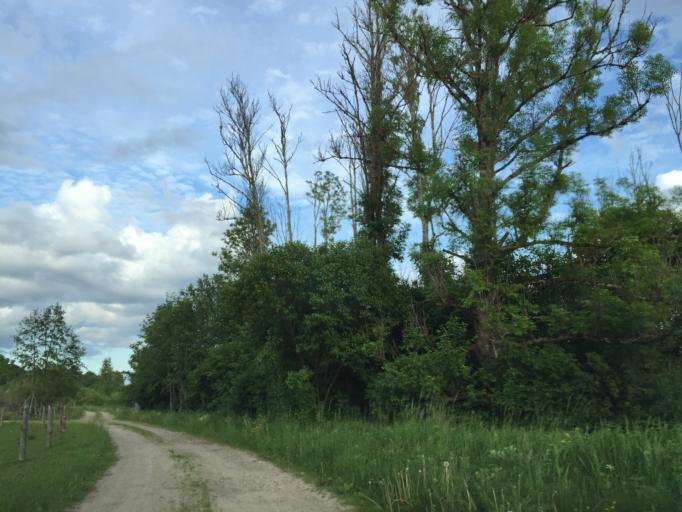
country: LV
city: Tireli
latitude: 56.8343
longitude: 23.5438
